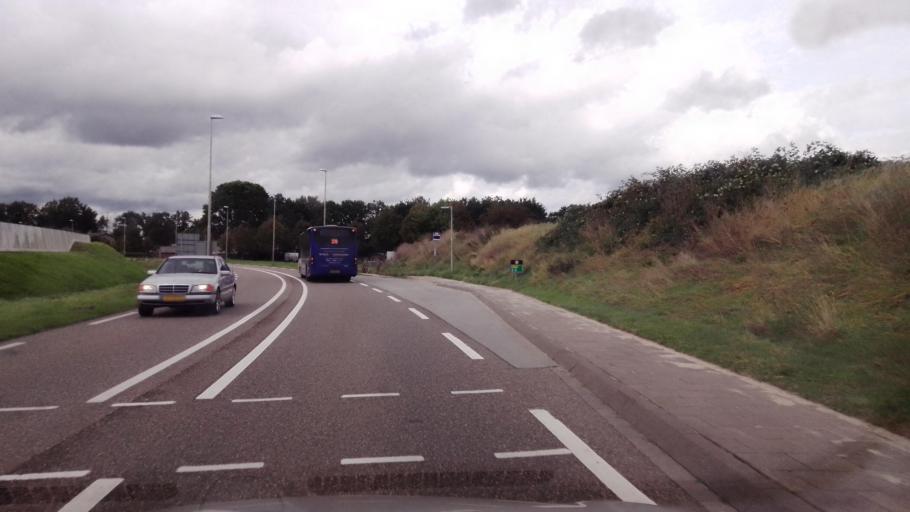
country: NL
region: Limburg
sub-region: Gemeente Venlo
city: Tegelen
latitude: 51.3648
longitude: 6.1198
